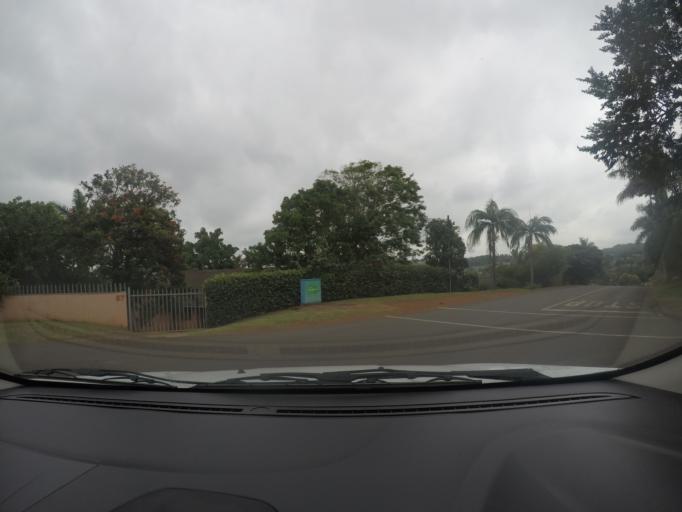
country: ZA
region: KwaZulu-Natal
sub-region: uThungulu District Municipality
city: Empangeni
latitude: -28.7664
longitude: 31.8885
